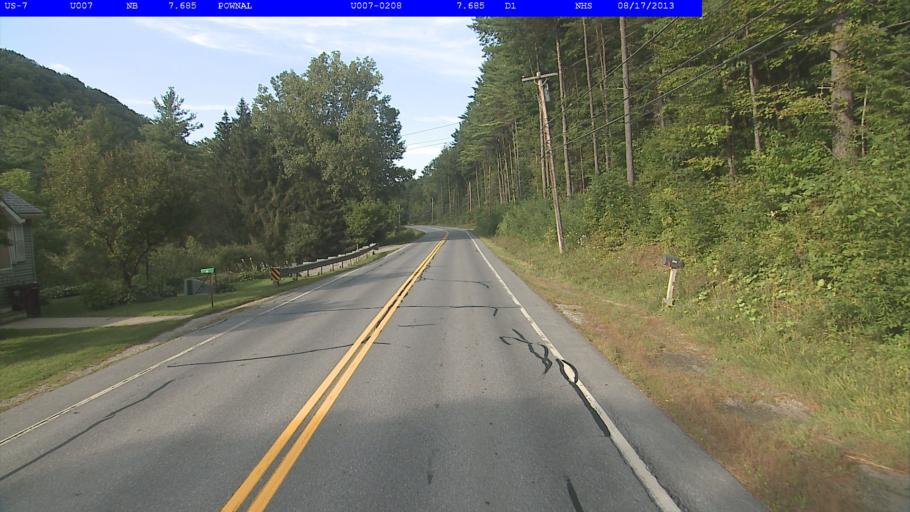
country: US
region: Vermont
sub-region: Bennington County
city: Bennington
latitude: 42.8334
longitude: -73.2003
